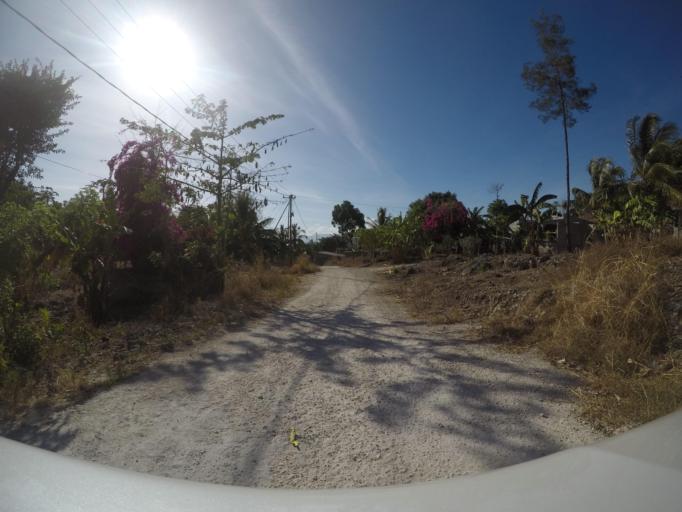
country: TL
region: Baucau
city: Baucau
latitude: -8.4508
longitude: 126.4302
